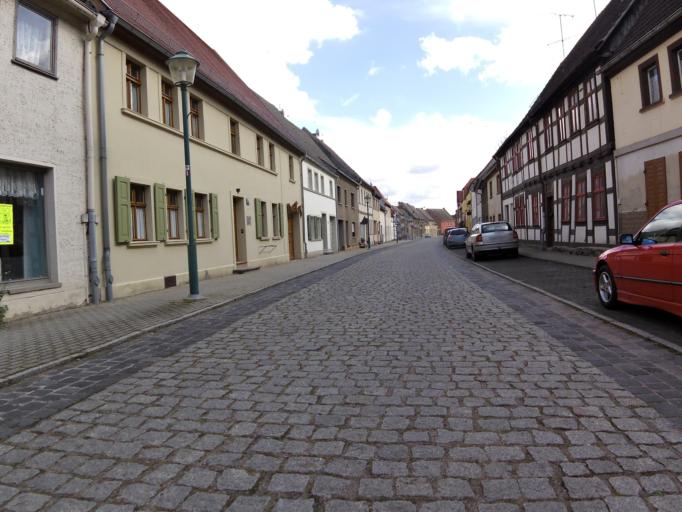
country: DE
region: Saxony-Anhalt
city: Worlitz
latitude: 51.8431
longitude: 12.4202
